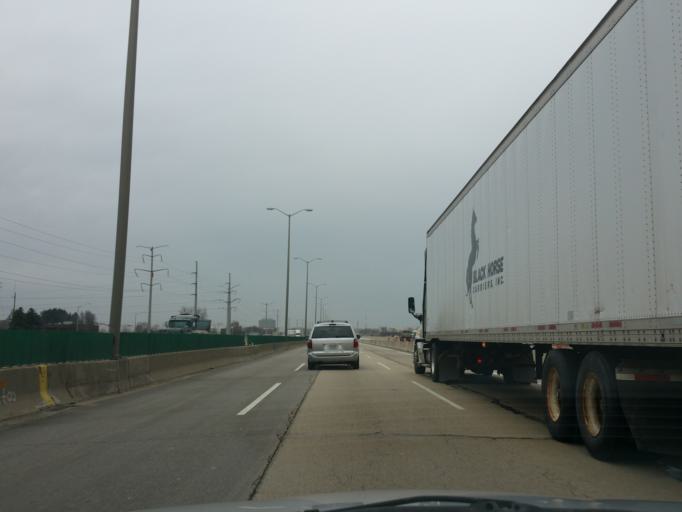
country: US
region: Illinois
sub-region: Cook County
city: Hoffman Estates
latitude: 42.0606
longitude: -88.0518
